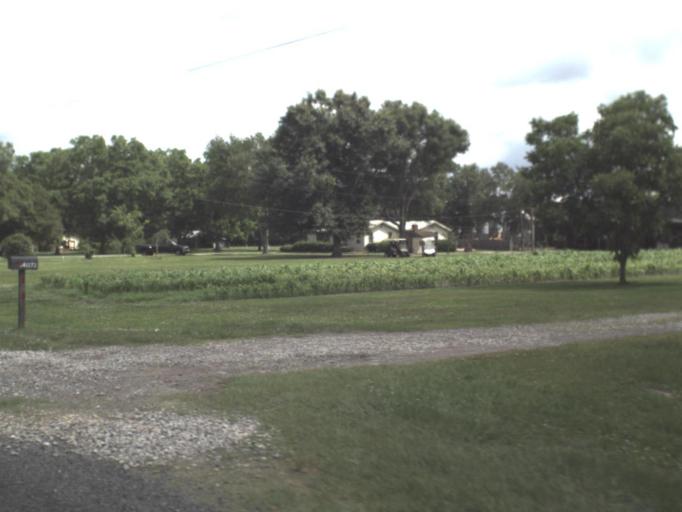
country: US
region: Florida
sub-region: Nassau County
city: Nassau Village-Ratliff
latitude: 30.5378
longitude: -81.8110
